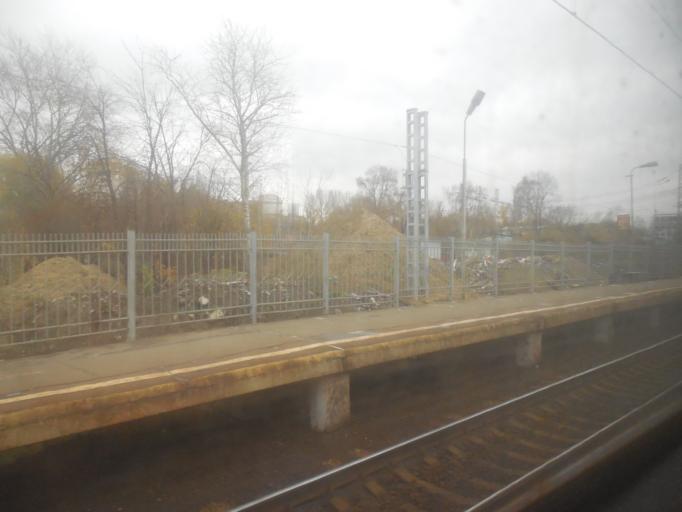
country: RU
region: Moskovskaya
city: Kastanayevo
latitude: 55.7420
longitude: 37.5122
